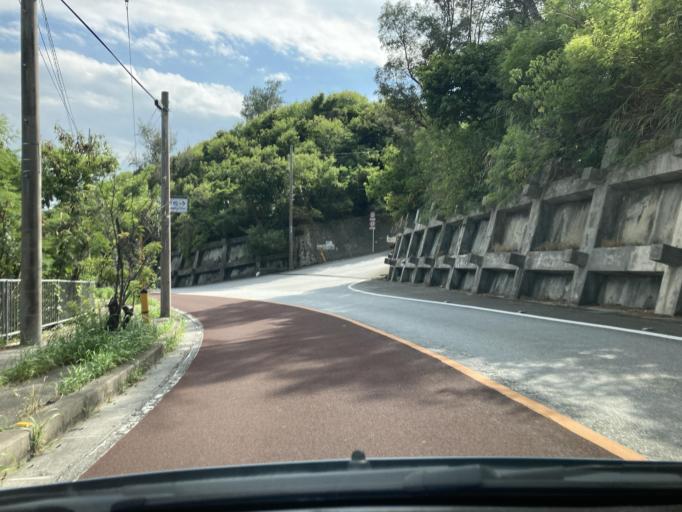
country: JP
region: Okinawa
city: Ginowan
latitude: 26.2673
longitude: 127.7856
